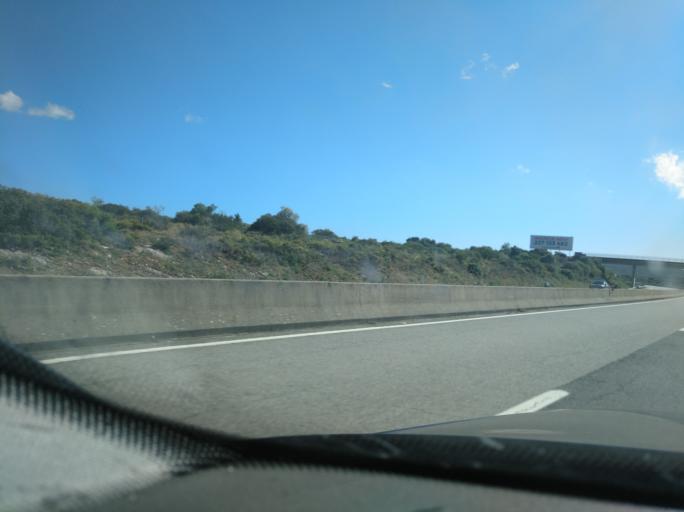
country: PT
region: Faro
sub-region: Olhao
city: Moncarapacho
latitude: 37.1328
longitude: -7.7551
